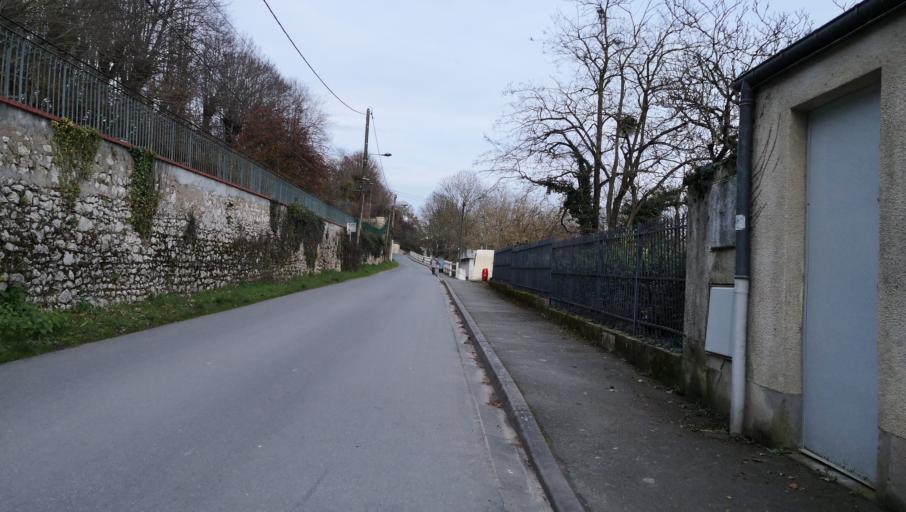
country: FR
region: Centre
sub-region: Departement du Loiret
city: La Chapelle-Saint-Mesmin
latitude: 47.8852
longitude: 1.8390
